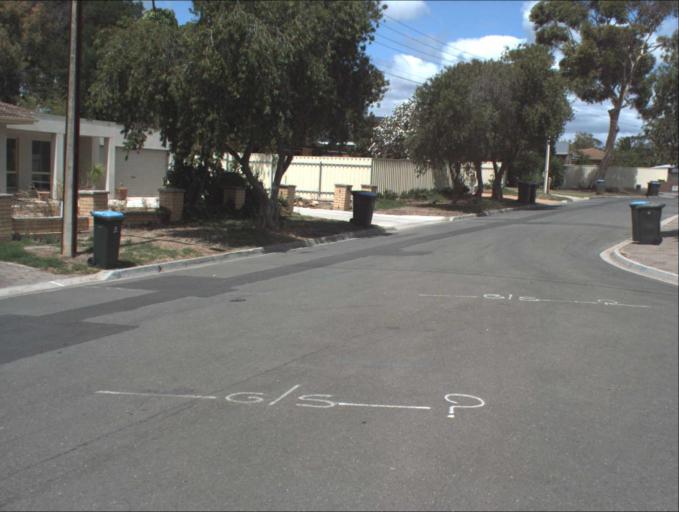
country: AU
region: South Australia
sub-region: Port Adelaide Enfield
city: Gilles Plains
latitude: -34.8442
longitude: 138.6503
